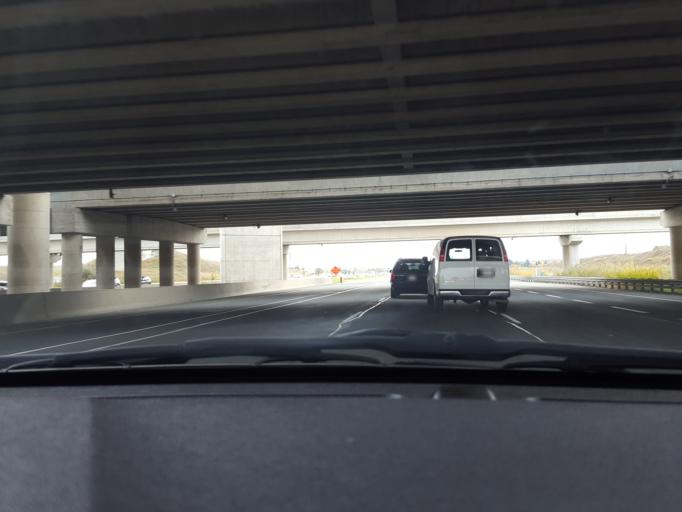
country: CA
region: Ontario
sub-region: York
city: Richmond Hill
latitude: 43.8394
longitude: -79.3684
